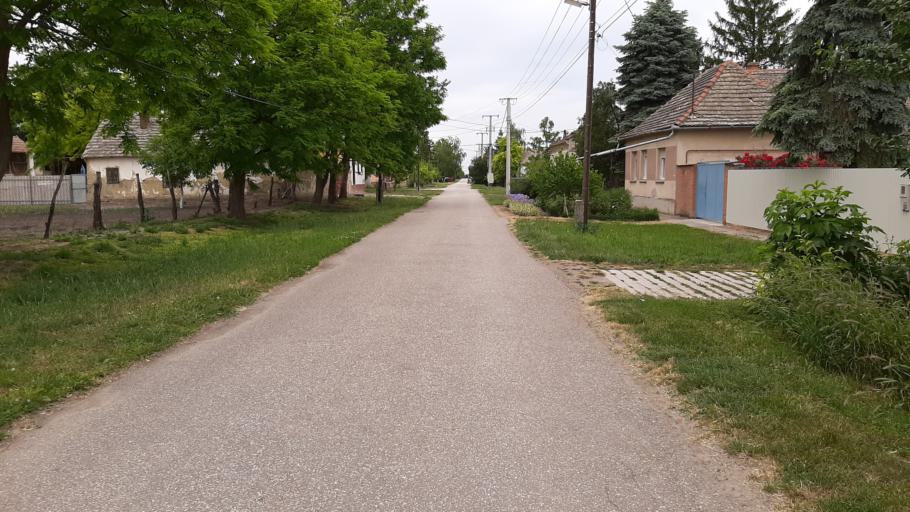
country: RO
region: Timis
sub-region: Comuna Beba Veche
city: Beba Veche
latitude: 46.1482
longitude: 20.2786
